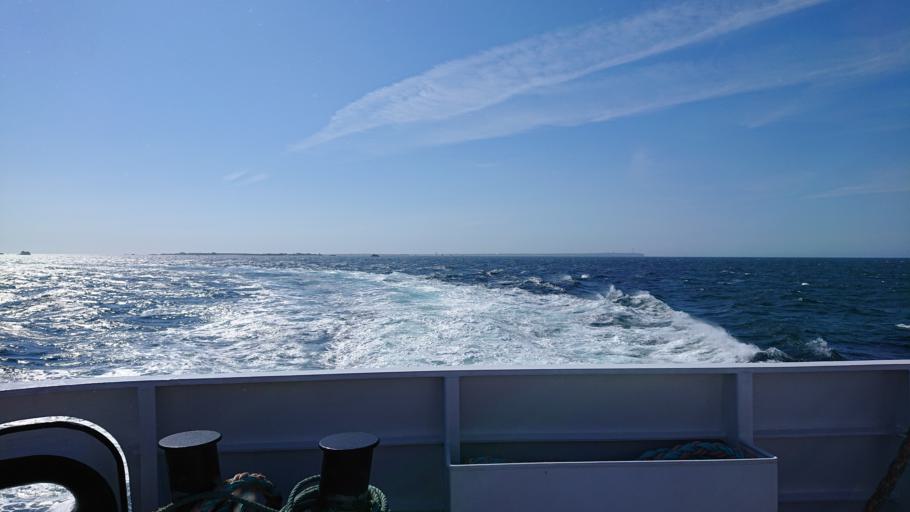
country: FR
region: Brittany
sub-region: Departement du Finistere
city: Le Conquet
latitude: 48.4154
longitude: -4.9424
